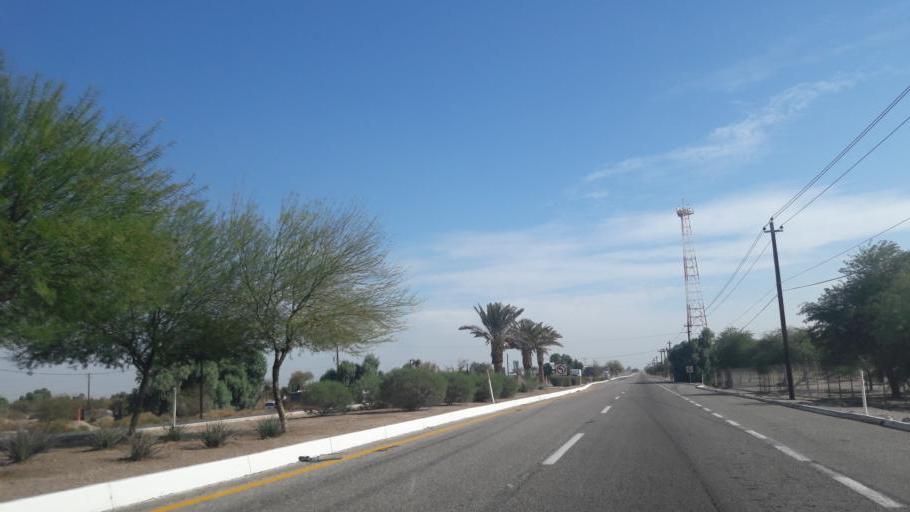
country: MX
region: Baja California
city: Progreso
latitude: 32.6025
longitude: -115.6585
